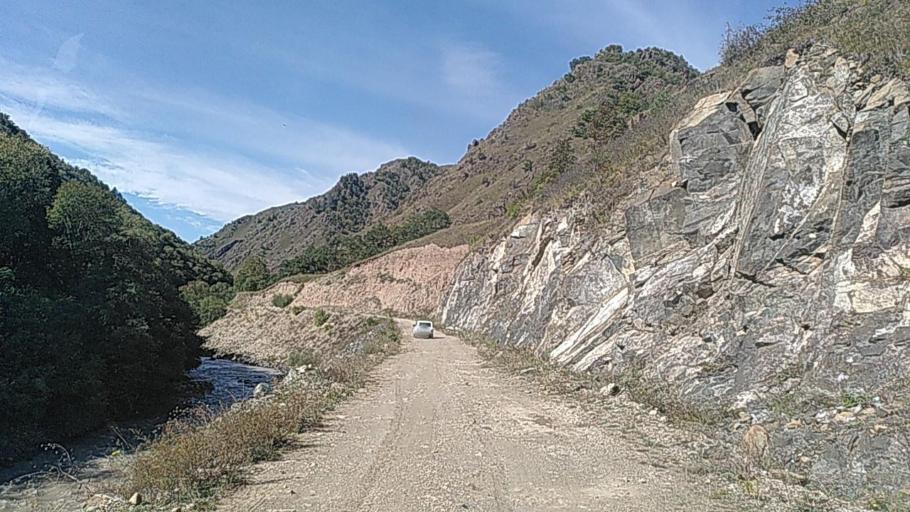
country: RU
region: Kabardino-Balkariya
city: Kamennomostskoye
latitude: 43.7225
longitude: 42.8608
